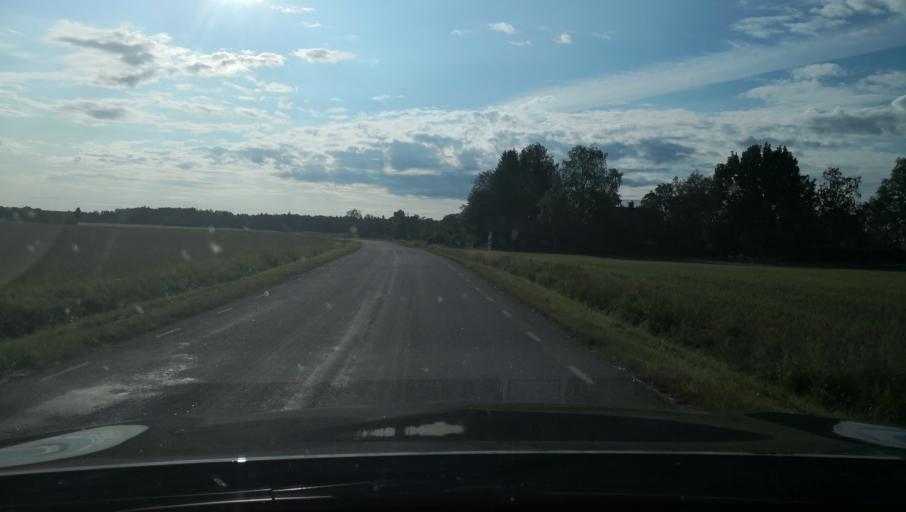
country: SE
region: Uppsala
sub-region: Osthammars Kommun
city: Osterbybruk
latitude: 60.0180
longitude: 17.9781
